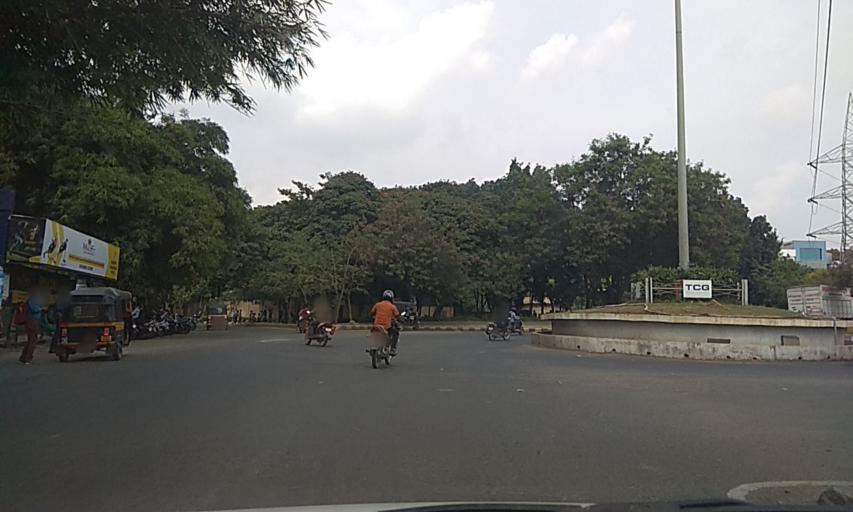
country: IN
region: Maharashtra
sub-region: Pune Division
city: Pimpri
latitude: 18.5933
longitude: 73.7078
